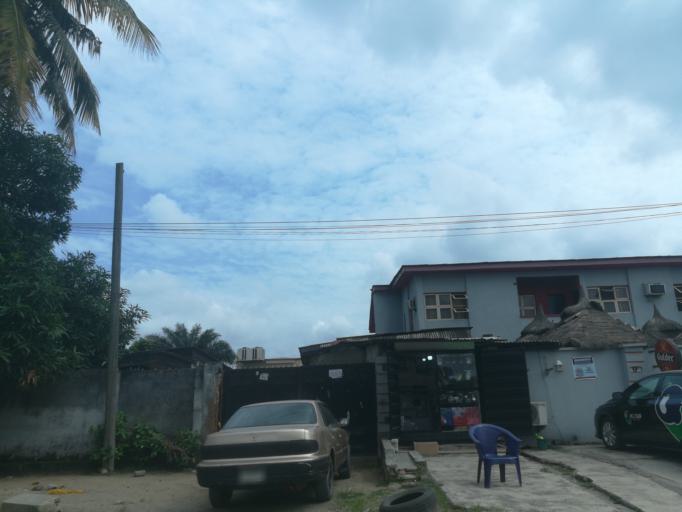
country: NG
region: Lagos
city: Somolu
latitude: 6.5470
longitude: 3.3876
